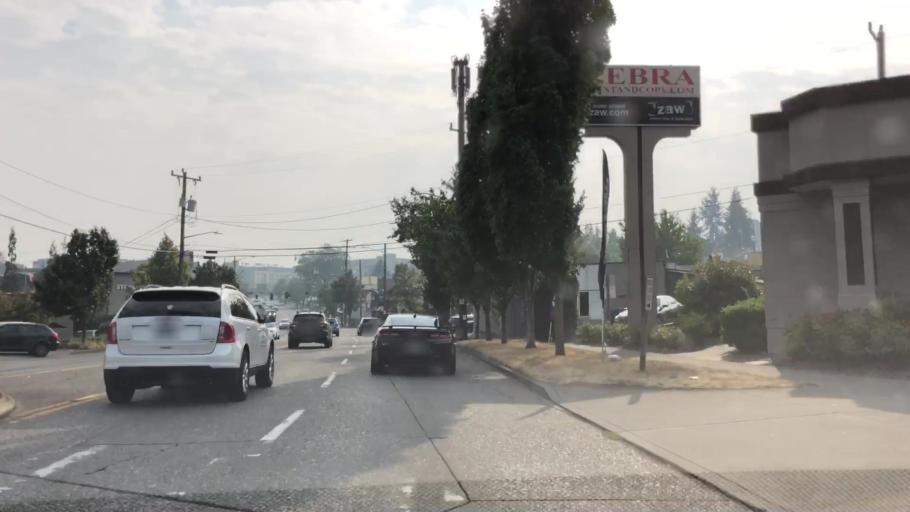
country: US
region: Washington
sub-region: King County
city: White Center
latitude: 47.5651
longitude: -122.3762
